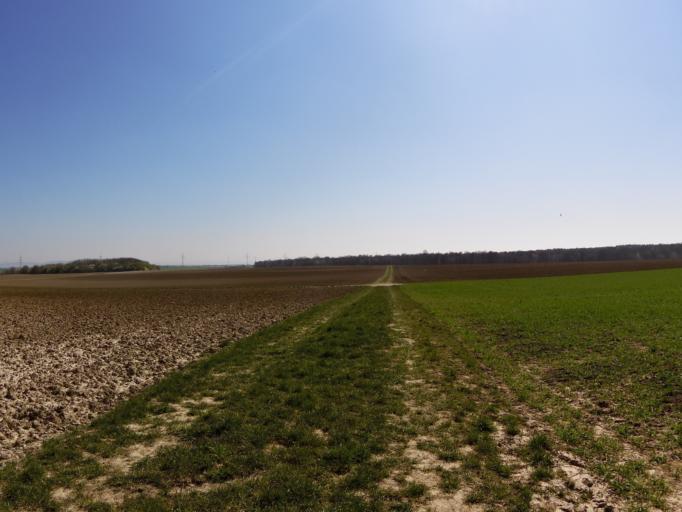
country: DE
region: Bavaria
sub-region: Regierungsbezirk Unterfranken
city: Kurnach
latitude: 49.8402
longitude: 10.0678
